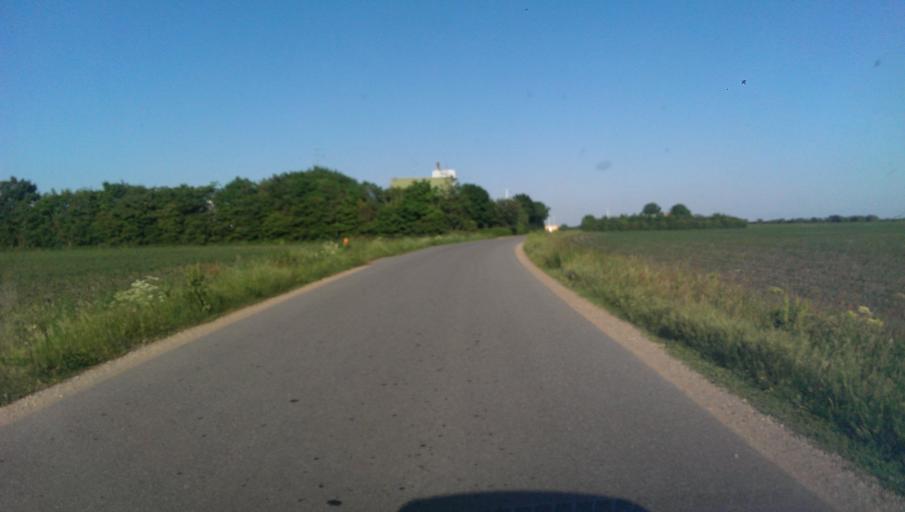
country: DK
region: South Denmark
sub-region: Esbjerg Kommune
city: Bramming
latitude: 55.5485
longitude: 8.6509
